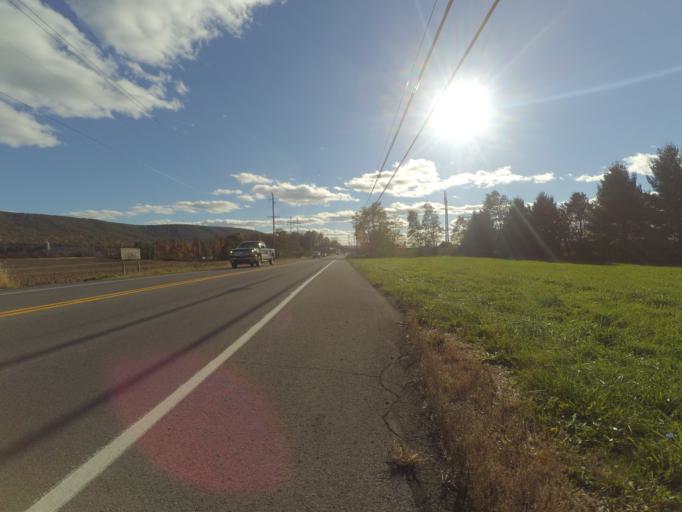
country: US
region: Pennsylvania
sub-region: Centre County
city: Houserville
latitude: 40.8479
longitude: -77.7926
